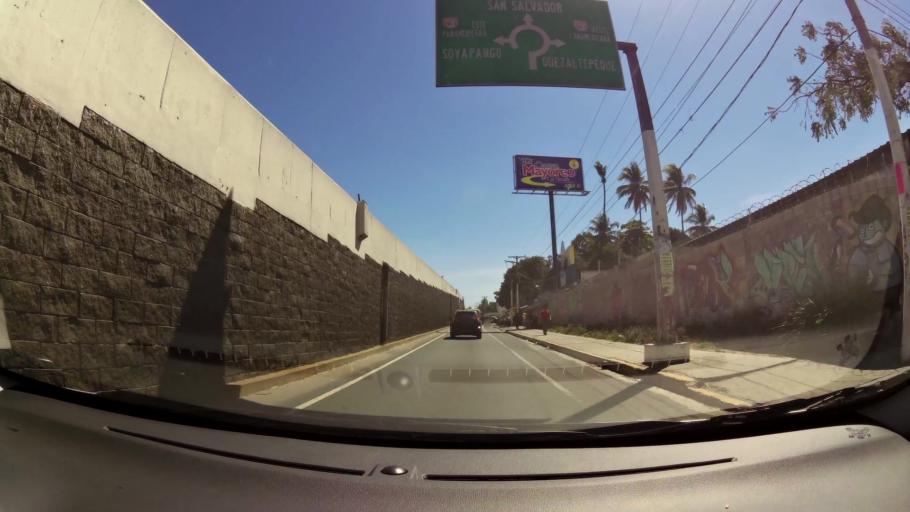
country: SV
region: San Salvador
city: Apopa
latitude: 13.7887
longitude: -89.1745
